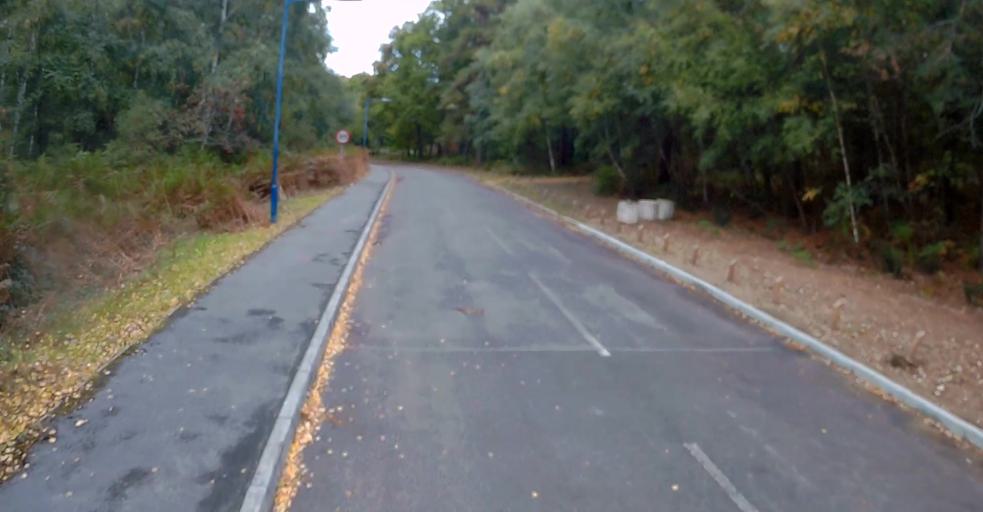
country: GB
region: England
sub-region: Surrey
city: Frimley
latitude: 51.3081
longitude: -0.6998
